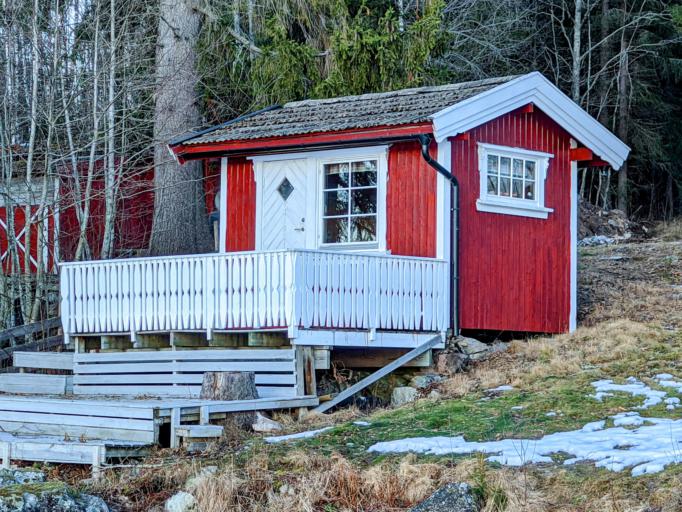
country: SE
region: Vaermland
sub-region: Eda Kommun
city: Charlottenberg
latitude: 60.1238
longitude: 12.3283
